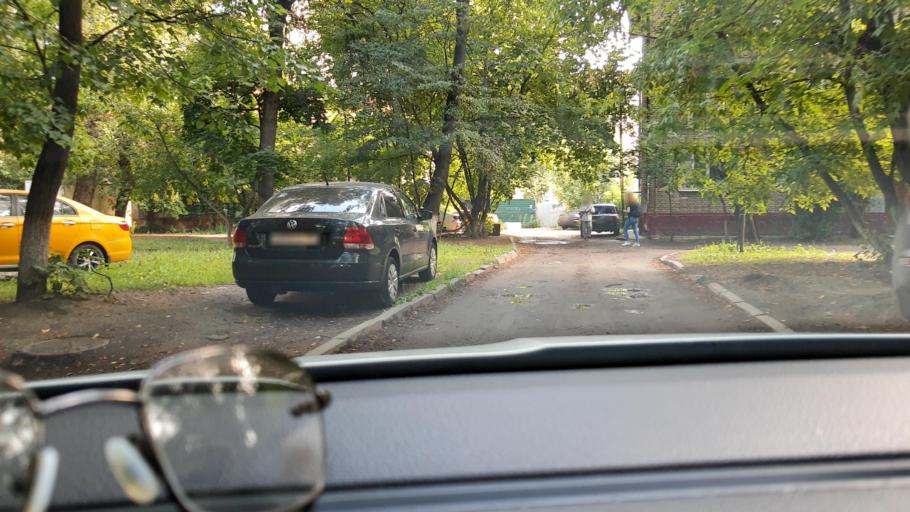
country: RU
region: Moskovskaya
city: Korolev
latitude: 55.9165
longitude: 37.8029
